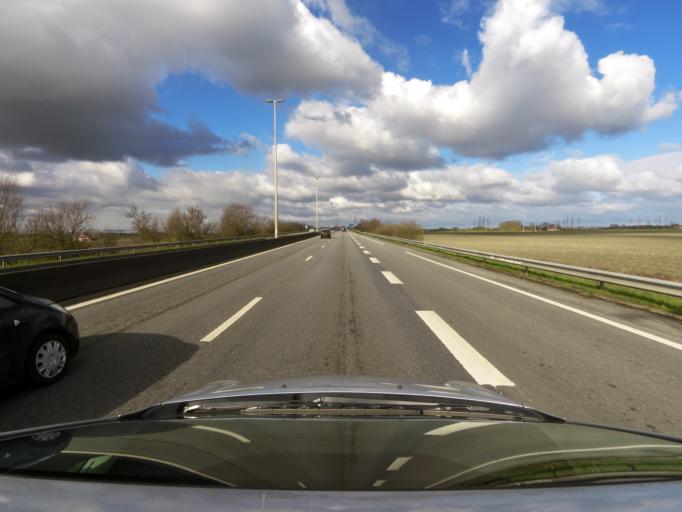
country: FR
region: Nord-Pas-de-Calais
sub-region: Departement du Nord
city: Bourbourg
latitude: 50.9587
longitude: 2.1791
